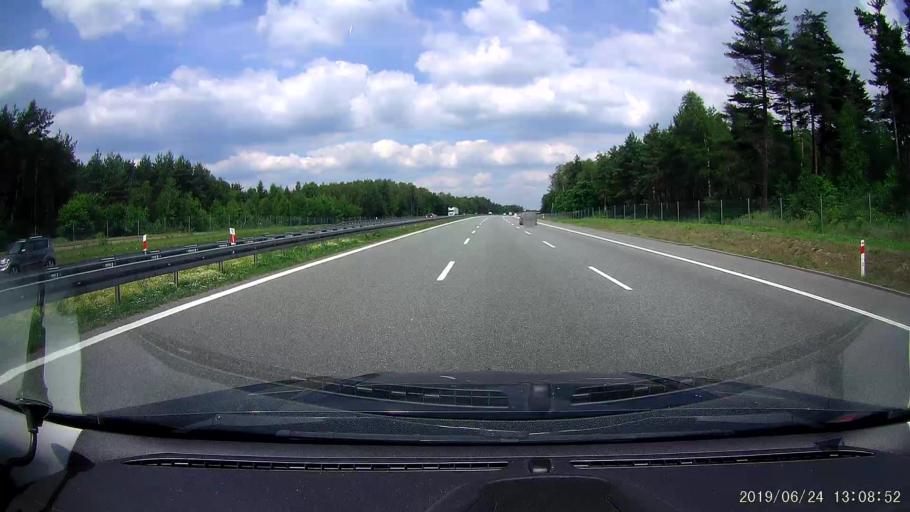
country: PL
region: Silesian Voivodeship
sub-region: Powiat rybnicki
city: Czerwionka-Leszczyny
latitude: 50.1849
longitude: 18.7079
